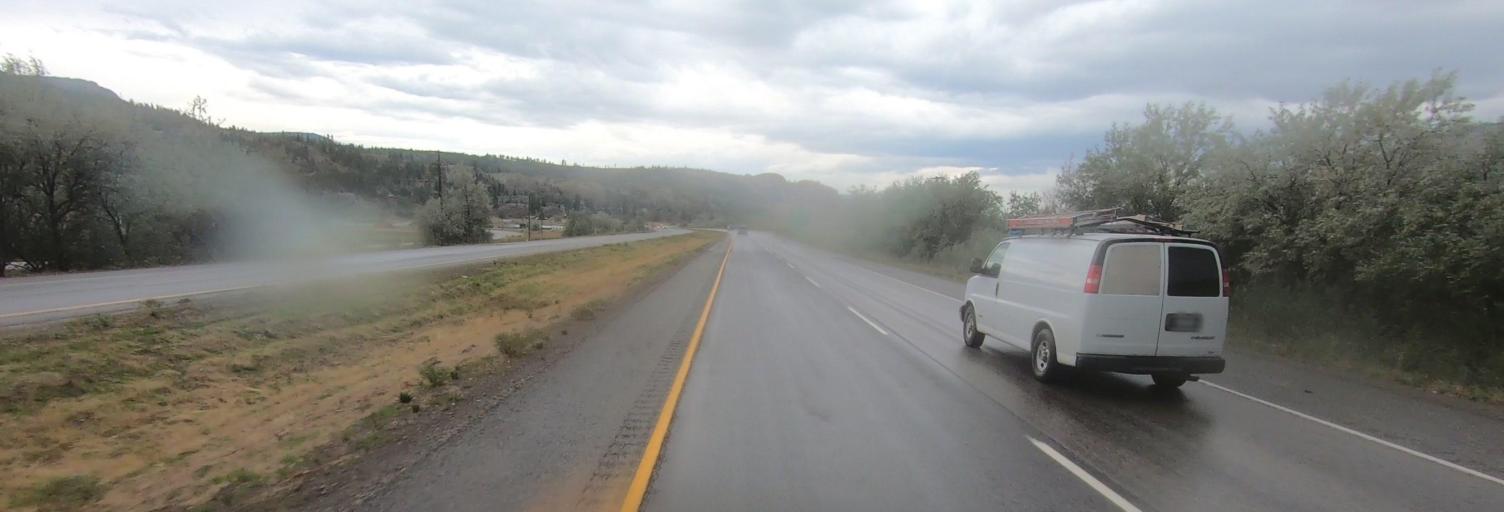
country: CA
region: British Columbia
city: Chase
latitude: 50.6495
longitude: -119.9743
